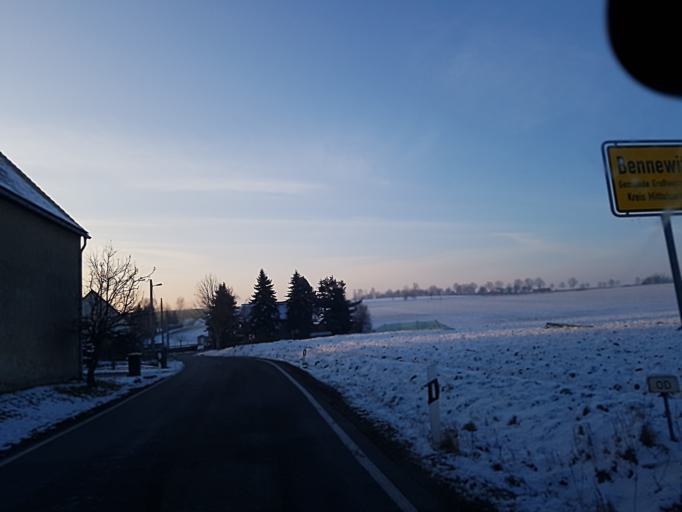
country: DE
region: Saxony
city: Grossweitzschen
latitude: 51.1803
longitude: 13.0369
